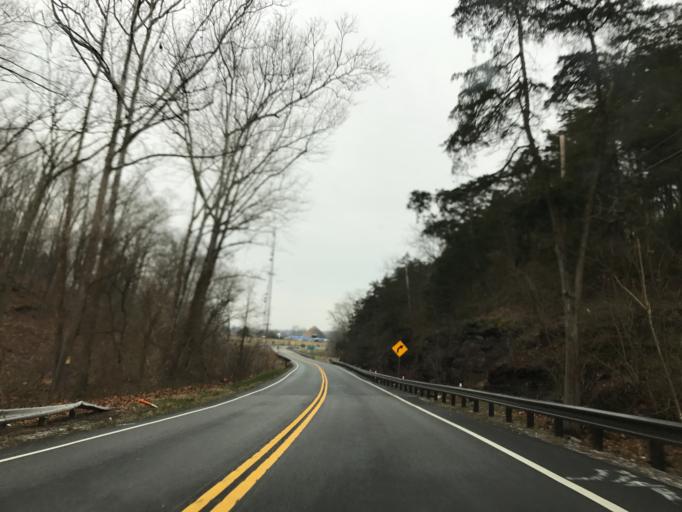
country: US
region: Maryland
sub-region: Carroll County
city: Taneytown
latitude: 39.6798
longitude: -77.2316
